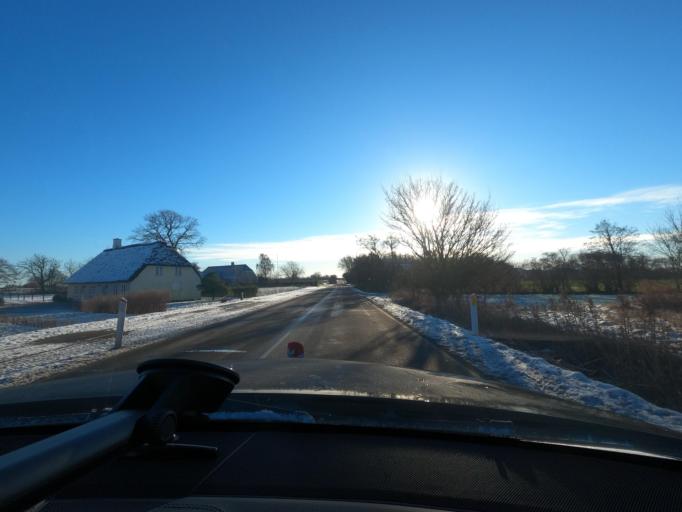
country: DK
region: South Denmark
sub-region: Sonderborg Kommune
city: Horuphav
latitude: 54.8772
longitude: 9.9952
